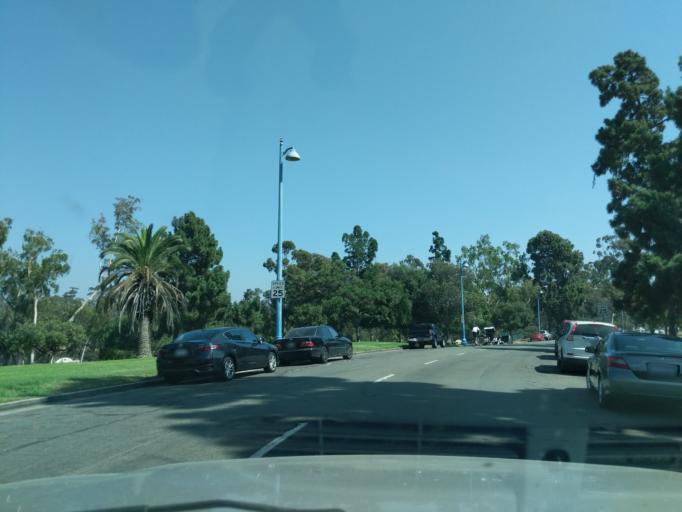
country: US
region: California
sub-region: San Diego County
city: San Diego
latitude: 32.7407
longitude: -117.1590
